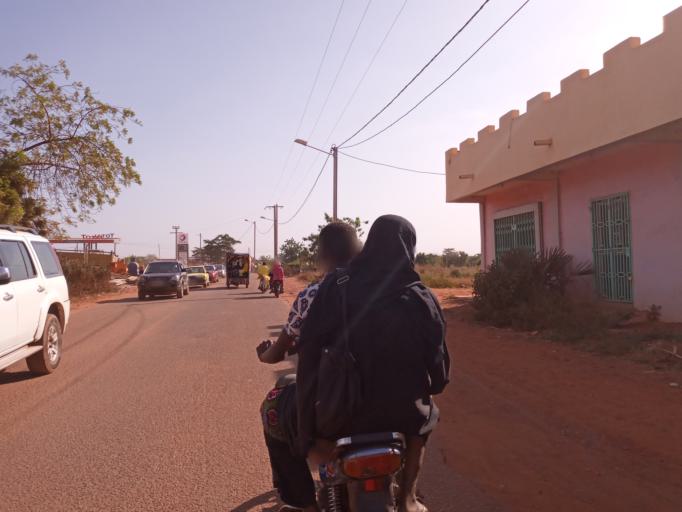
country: ML
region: Bamako
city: Bamako
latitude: 12.6257
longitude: -7.9553
